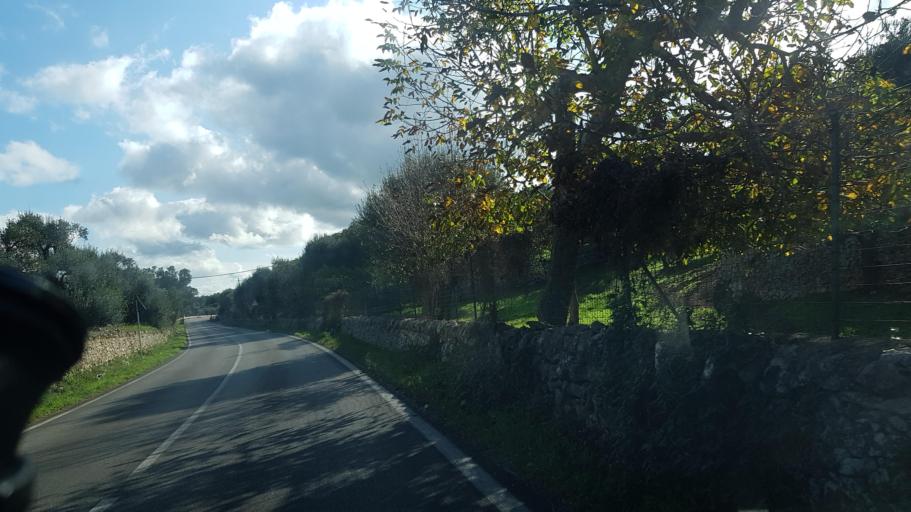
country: IT
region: Apulia
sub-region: Provincia di Brindisi
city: Ostuni
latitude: 40.6938
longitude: 17.5878
